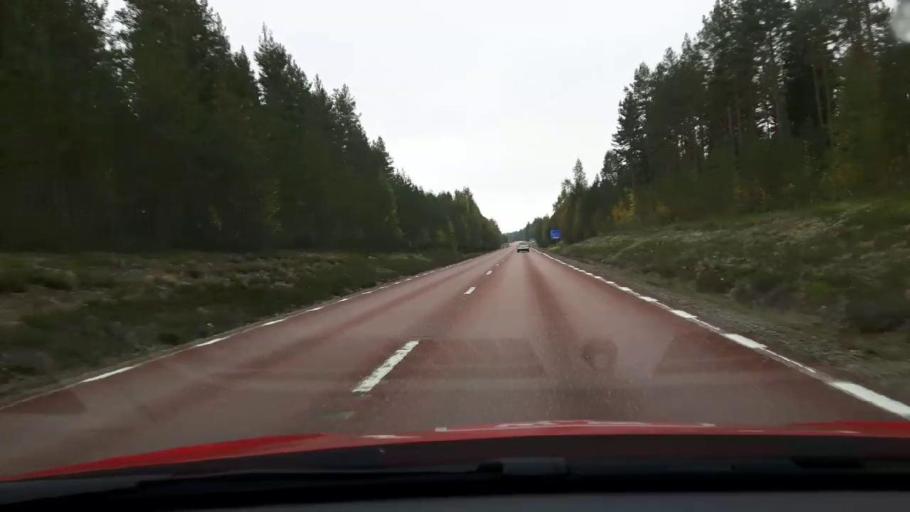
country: SE
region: Gaevleborg
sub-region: Ljusdals Kommun
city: Farila
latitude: 61.8122
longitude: 15.7684
